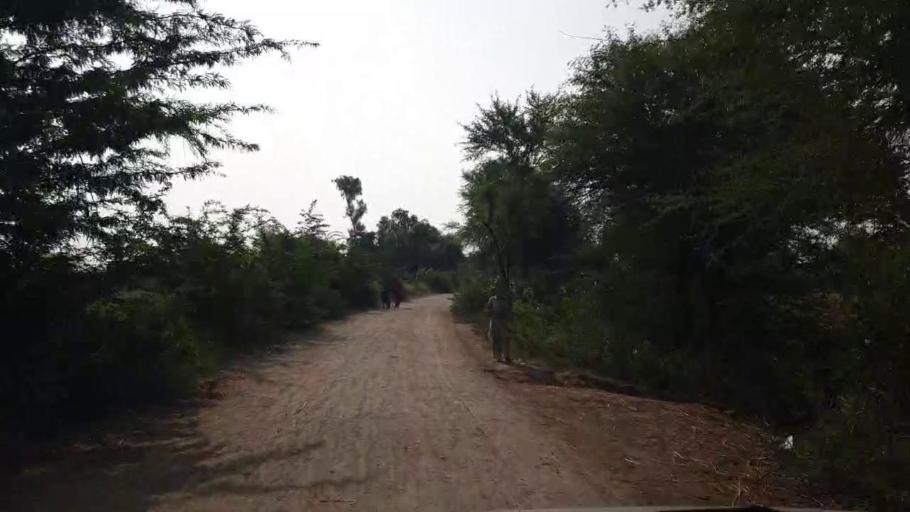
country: PK
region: Sindh
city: Rajo Khanani
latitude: 24.9135
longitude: 68.9192
